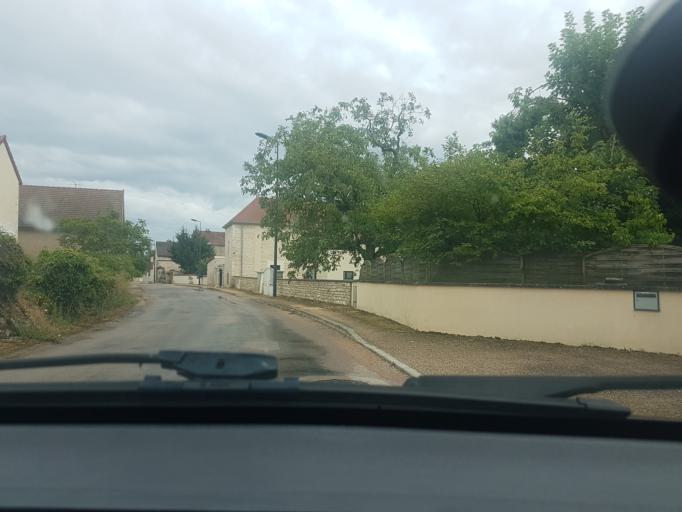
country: FR
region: Bourgogne
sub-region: Departement de Saone-et-Loire
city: Fontaines
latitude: 46.8599
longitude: 4.7602
